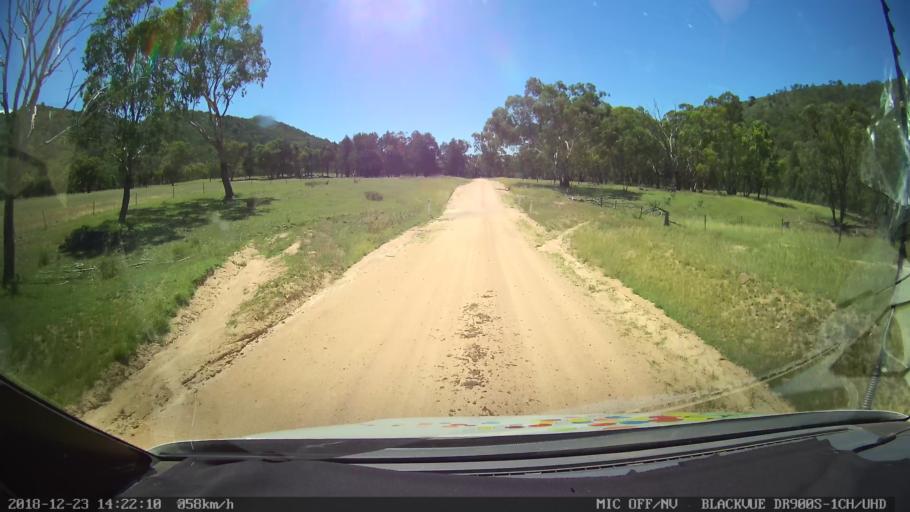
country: AU
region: New South Wales
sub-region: Tamworth Municipality
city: Manilla
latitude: -30.6430
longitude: 150.9750
